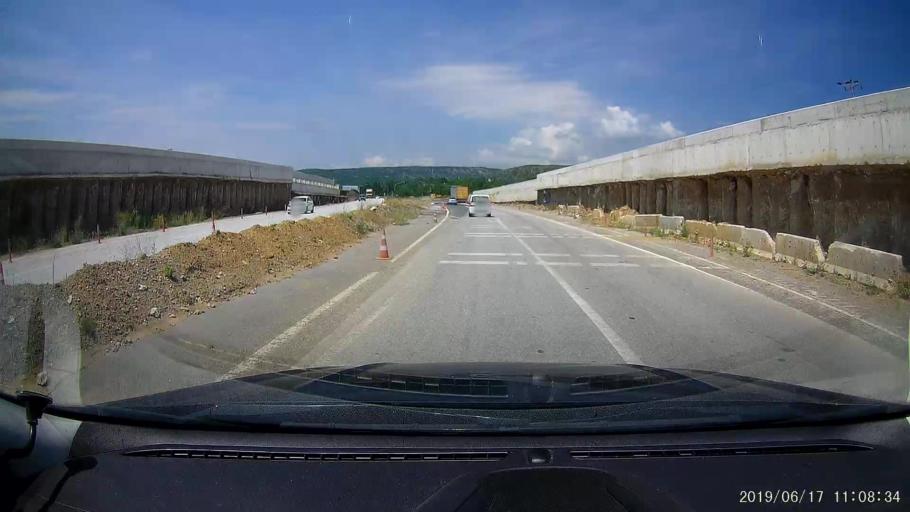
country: TR
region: Kastamonu
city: Tosya
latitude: 41.0009
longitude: 34.0350
